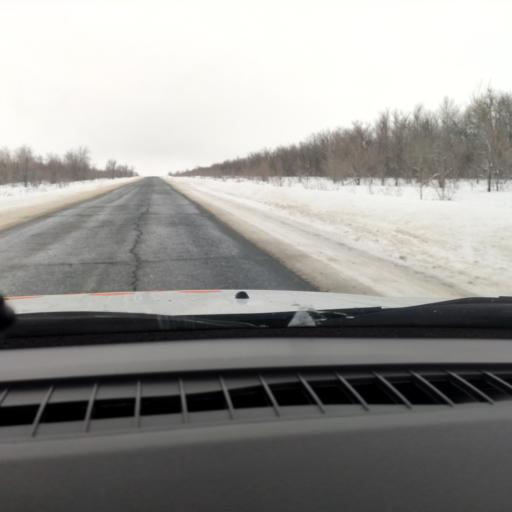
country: RU
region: Samara
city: Mayskoye
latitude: 52.4422
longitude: 50.5366
